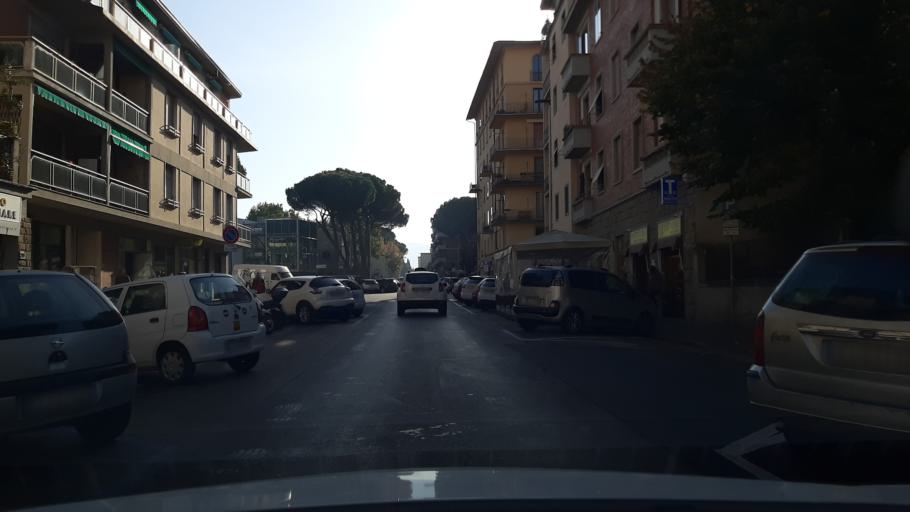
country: IT
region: Tuscany
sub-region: Province of Florence
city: Fiesole
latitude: 43.7822
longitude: 11.2893
